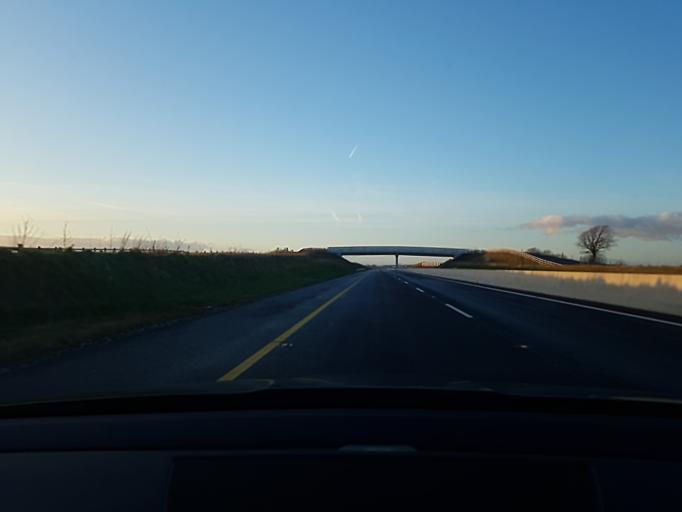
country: IE
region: Connaught
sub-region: County Galway
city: Tuam
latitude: 53.4637
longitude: -8.8546
